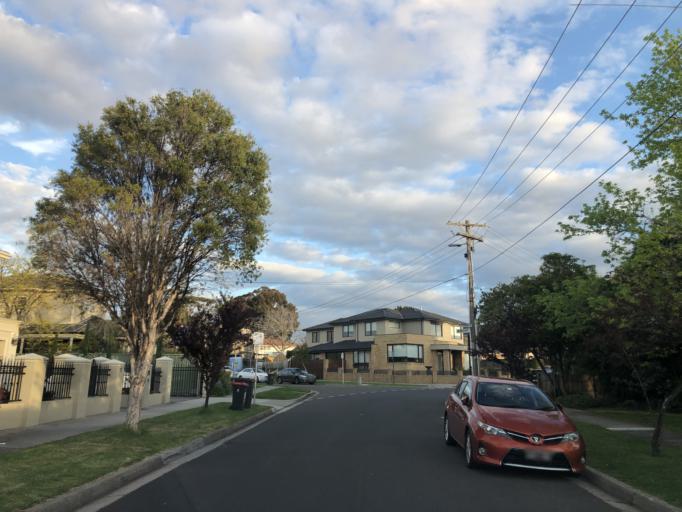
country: AU
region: Victoria
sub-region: Monash
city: Ashwood
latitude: -37.8740
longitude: 145.1251
